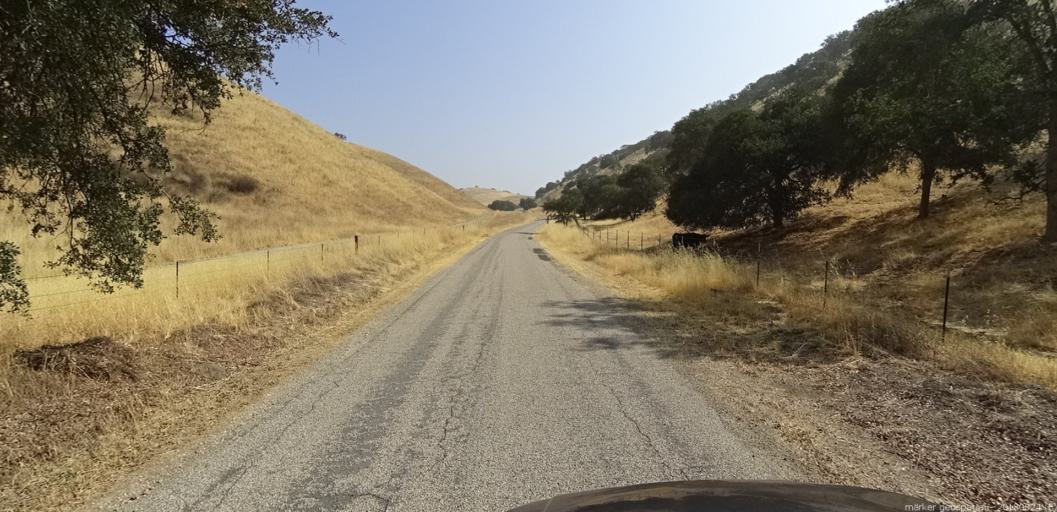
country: US
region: California
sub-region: San Luis Obispo County
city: San Miguel
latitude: 35.9080
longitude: -120.7189
